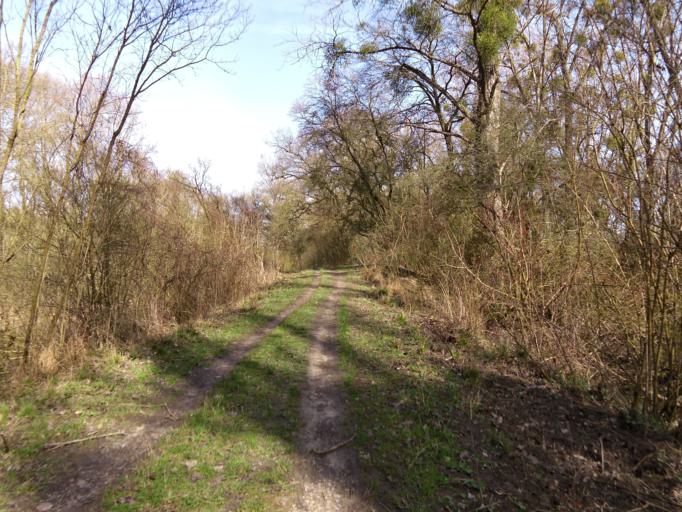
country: DE
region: Rheinland-Pfalz
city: Gimbsheim
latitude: 49.8163
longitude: 8.4153
